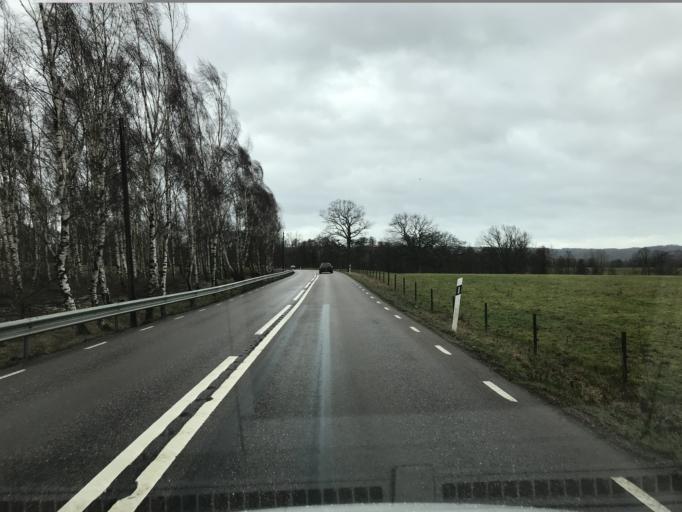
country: SE
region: Skane
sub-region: Klippans Kommun
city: Klippan
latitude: 56.1118
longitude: 13.1786
